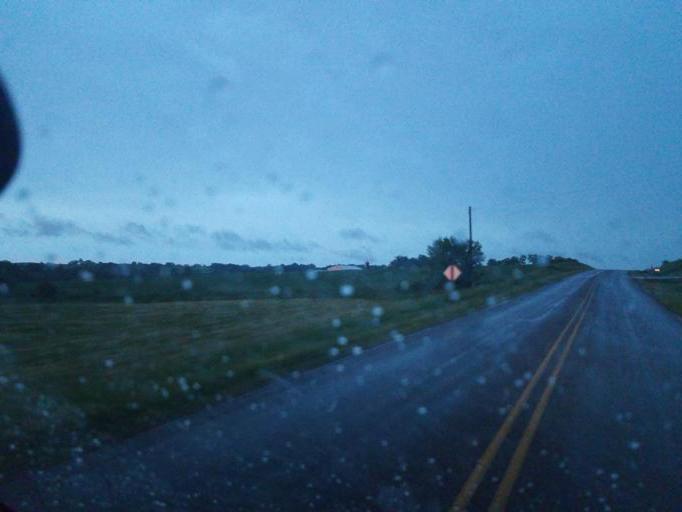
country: US
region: Wisconsin
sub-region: Vernon County
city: Hillsboro
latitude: 43.5859
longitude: -90.3579
